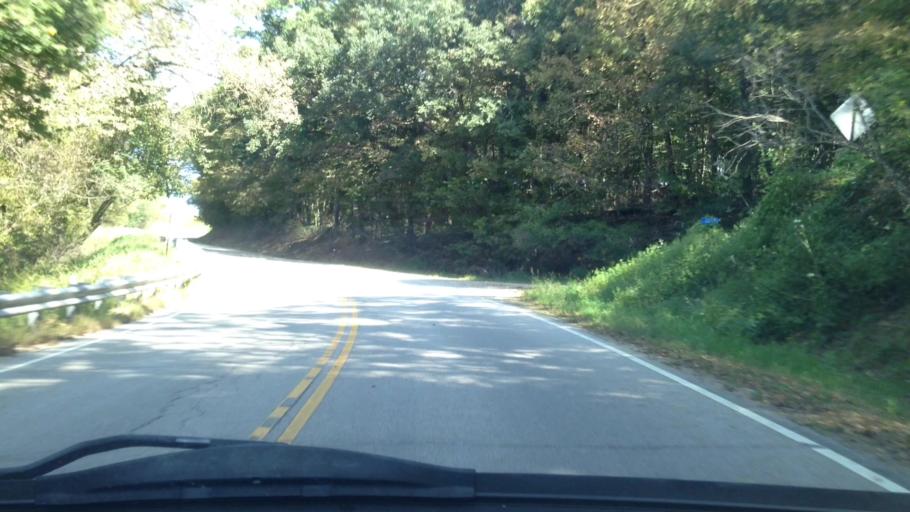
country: US
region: Minnesota
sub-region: Fillmore County
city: Rushford
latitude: 43.6868
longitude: -91.7797
